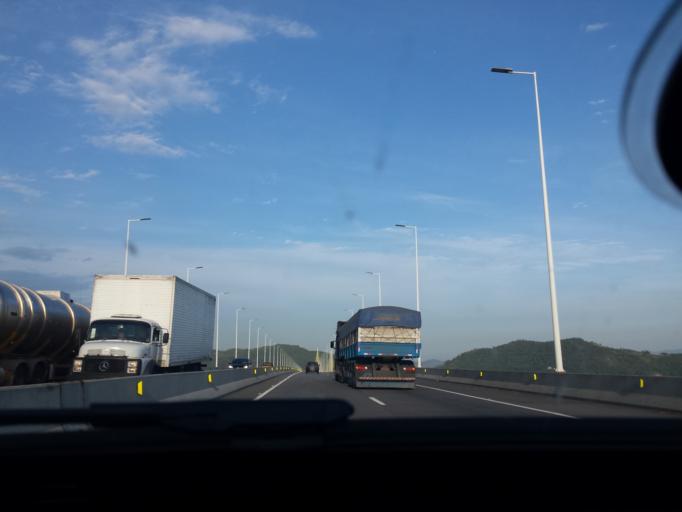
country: BR
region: Santa Catarina
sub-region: Laguna
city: Laguna
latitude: -28.4399
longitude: -48.8269
